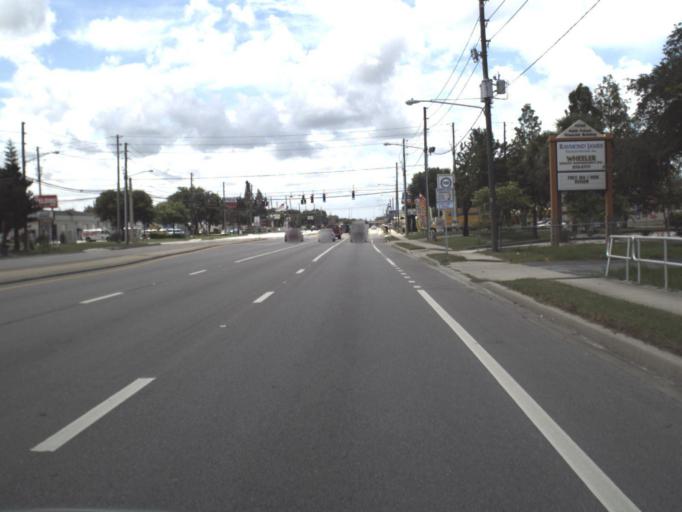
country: US
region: Florida
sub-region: Pinellas County
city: Pinellas Park
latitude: 27.8734
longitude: -82.7004
